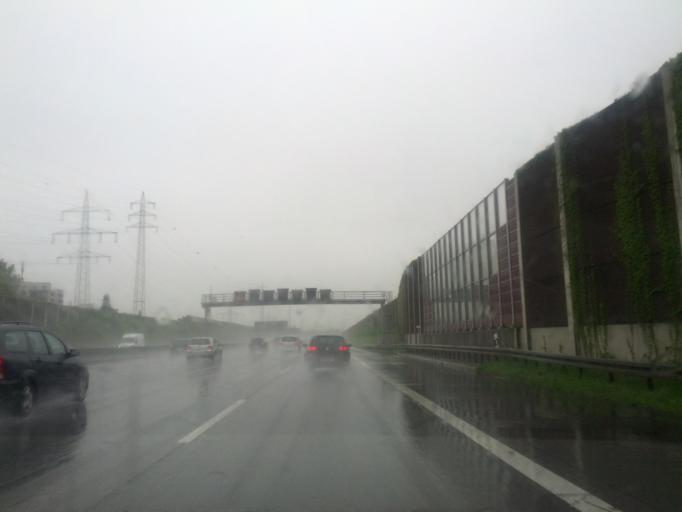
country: DE
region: North Rhine-Westphalia
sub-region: Regierungsbezirk Koln
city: Ostheim
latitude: 50.9322
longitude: 7.0519
